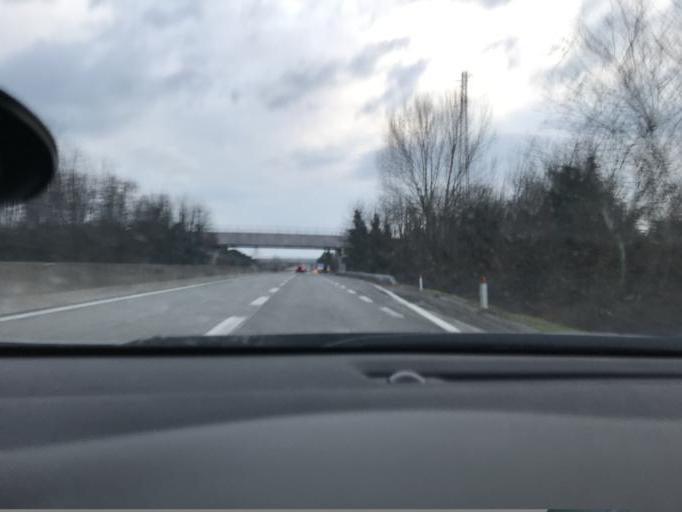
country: IT
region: Umbria
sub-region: Provincia di Perugia
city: Petrignano
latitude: 43.1173
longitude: 12.5103
